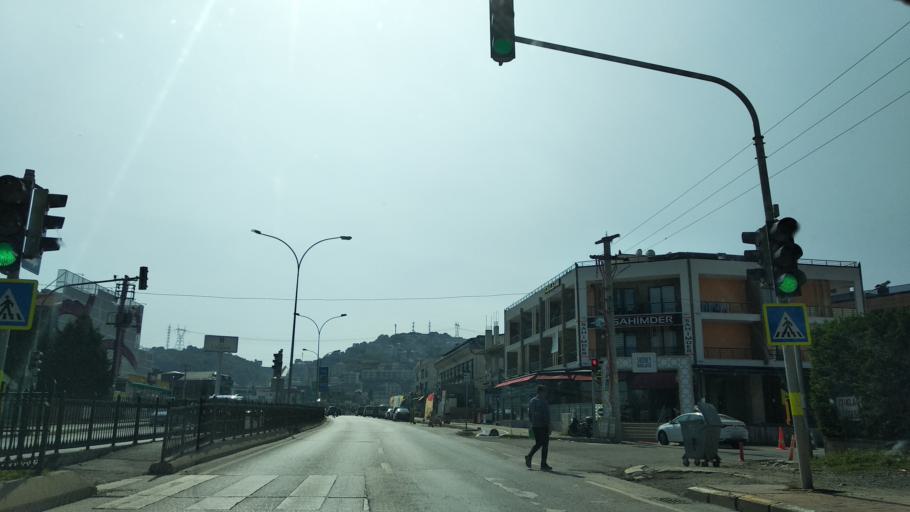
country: TR
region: Sakarya
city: Adapazari
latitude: 40.7626
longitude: 30.3631
